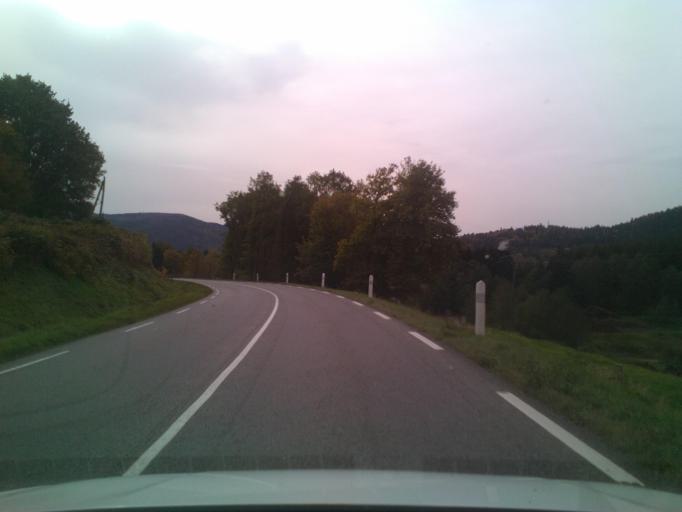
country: FR
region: Lorraine
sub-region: Departement des Vosges
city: Saint-Ame
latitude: 48.0436
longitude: 6.6813
